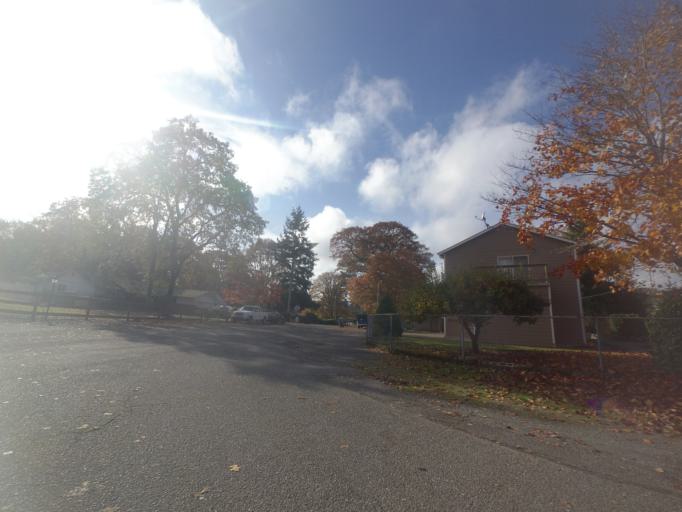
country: US
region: Washington
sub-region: Pierce County
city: Lakewood
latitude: 47.1763
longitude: -122.5131
